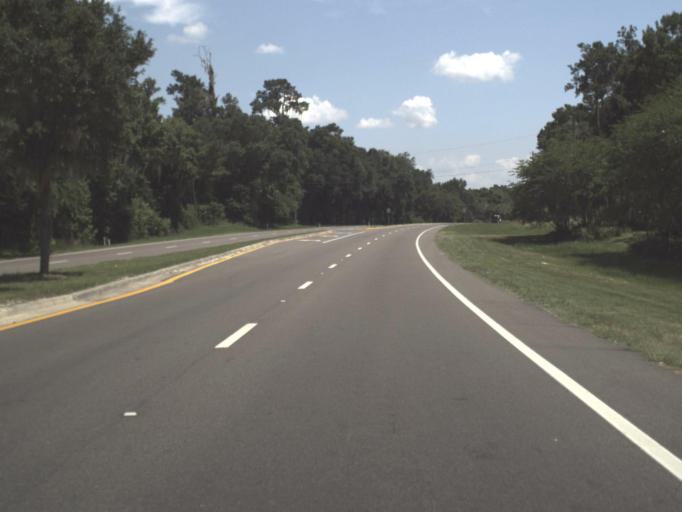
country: US
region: Florida
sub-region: Alachua County
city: Gainesville
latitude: 29.6246
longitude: -82.2582
